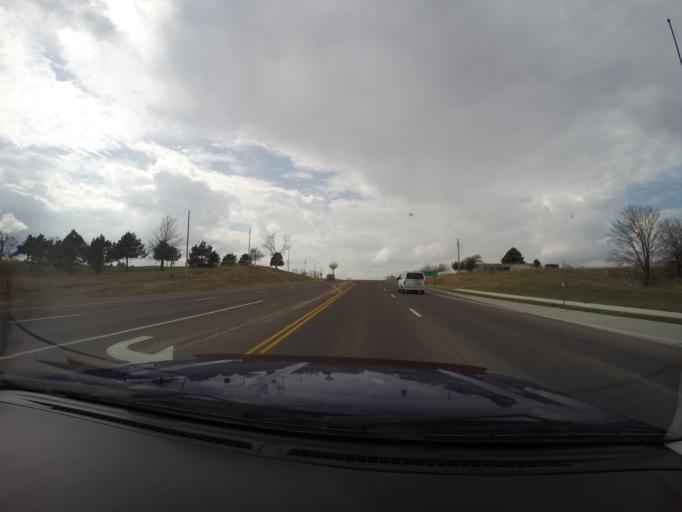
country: US
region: Kansas
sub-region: Pottawatomie County
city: Wamego
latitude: 39.2103
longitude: -96.3228
